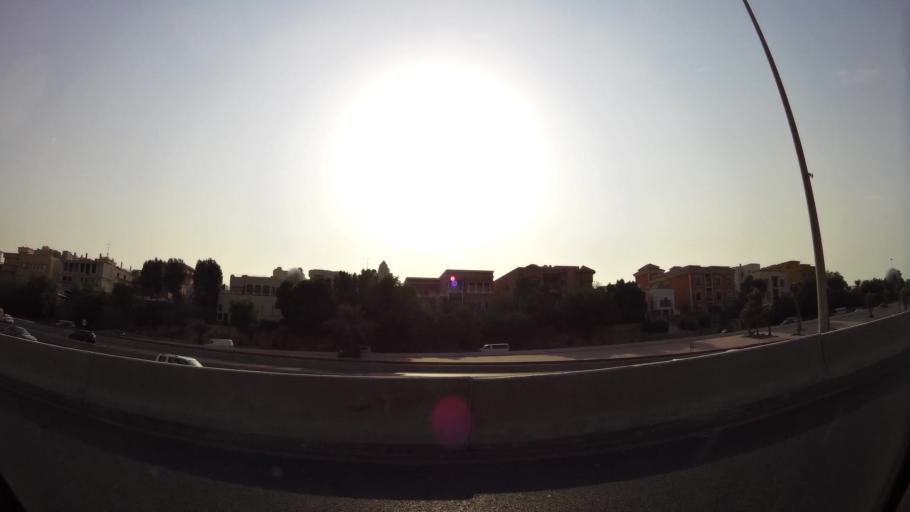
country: KW
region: Muhafazat Hawalli
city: Hawalli
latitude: 29.3213
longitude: 48.0138
